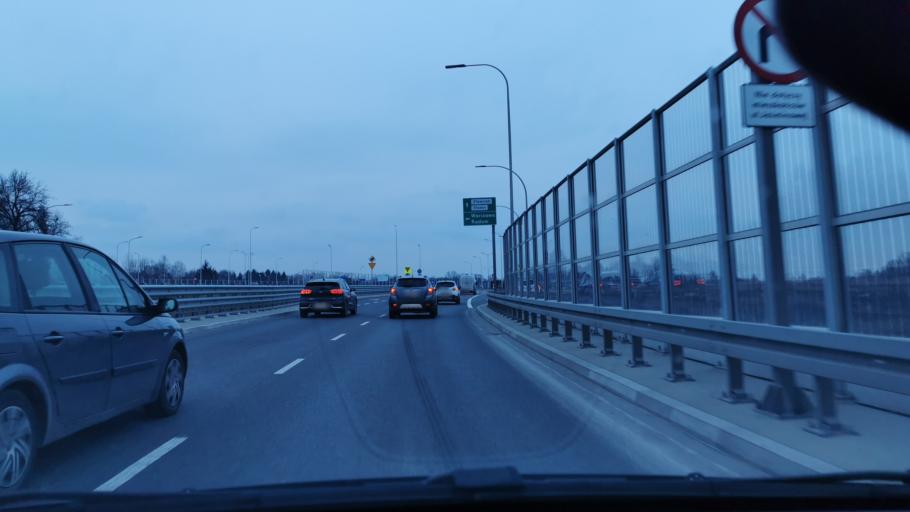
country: PL
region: Lublin Voivodeship
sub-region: Powiat lubelski
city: Lublin
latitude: 51.2548
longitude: 22.5056
